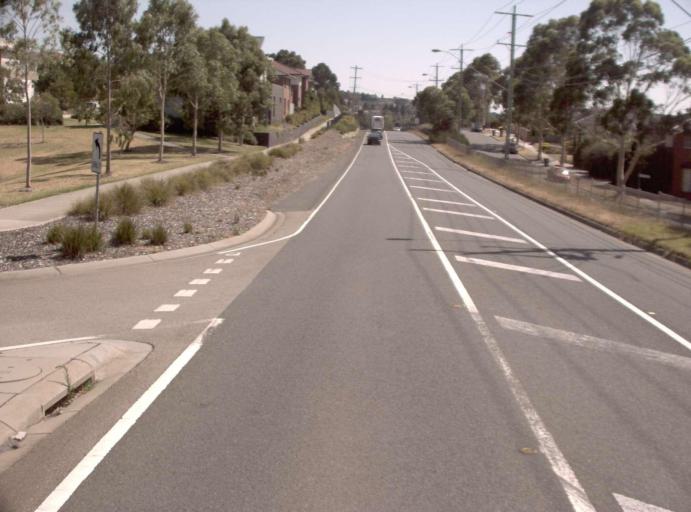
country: AU
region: Victoria
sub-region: Monash
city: Mulgrave
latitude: -37.9268
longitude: 145.1947
